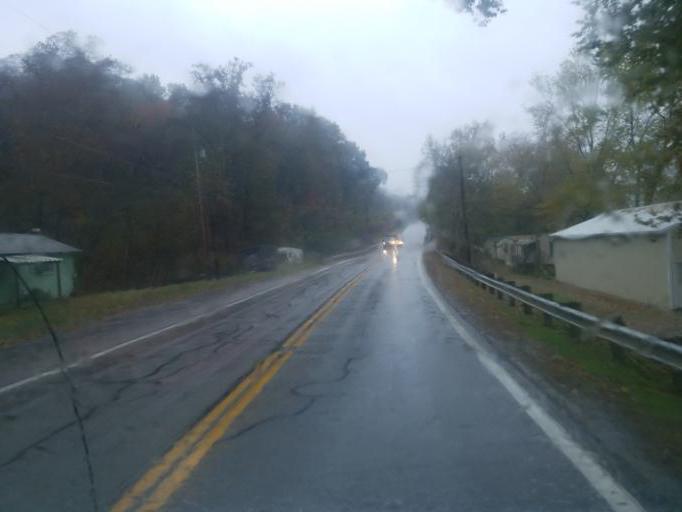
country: US
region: Ohio
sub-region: Morgan County
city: McConnelsville
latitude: 39.7687
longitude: -81.8952
